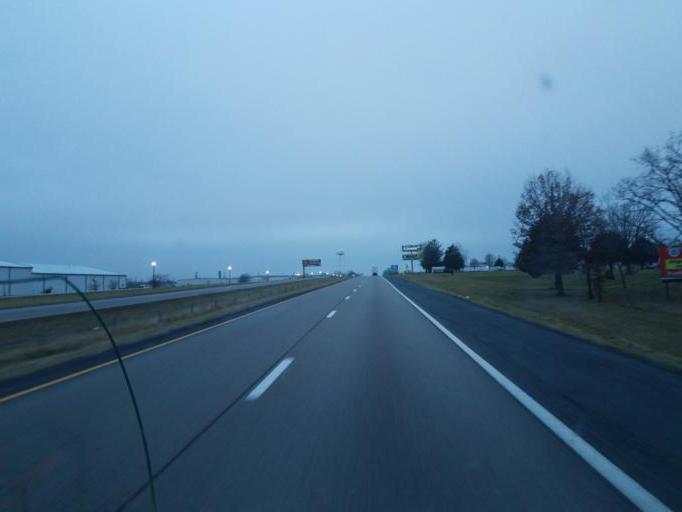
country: US
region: Missouri
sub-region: Phelps County
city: Saint James
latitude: 38.0130
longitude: -91.5937
